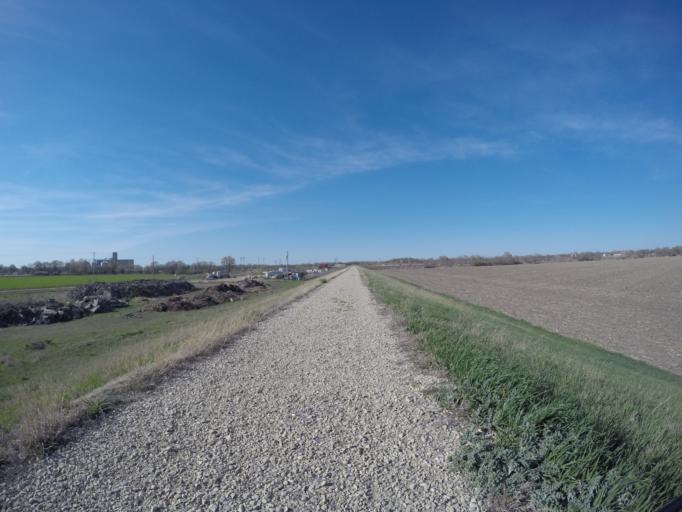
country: US
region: Kansas
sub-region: Saline County
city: Salina
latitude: 38.8500
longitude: -97.5748
